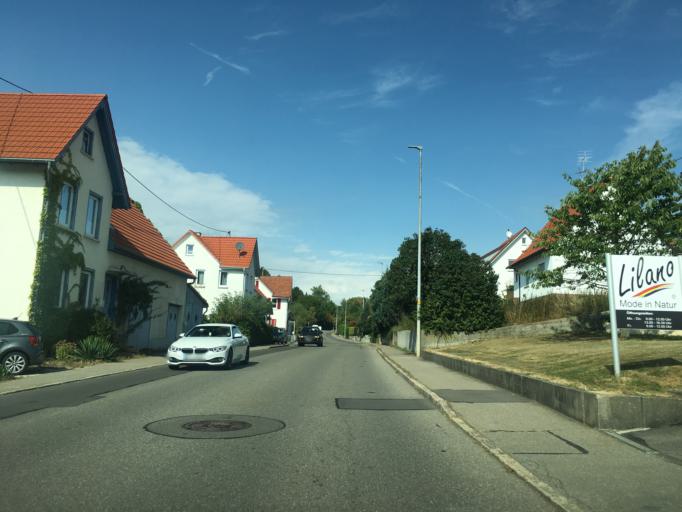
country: DE
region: Baden-Wuerttemberg
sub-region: Tuebingen Region
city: Gomaringen
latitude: 48.4381
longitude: 9.1480
